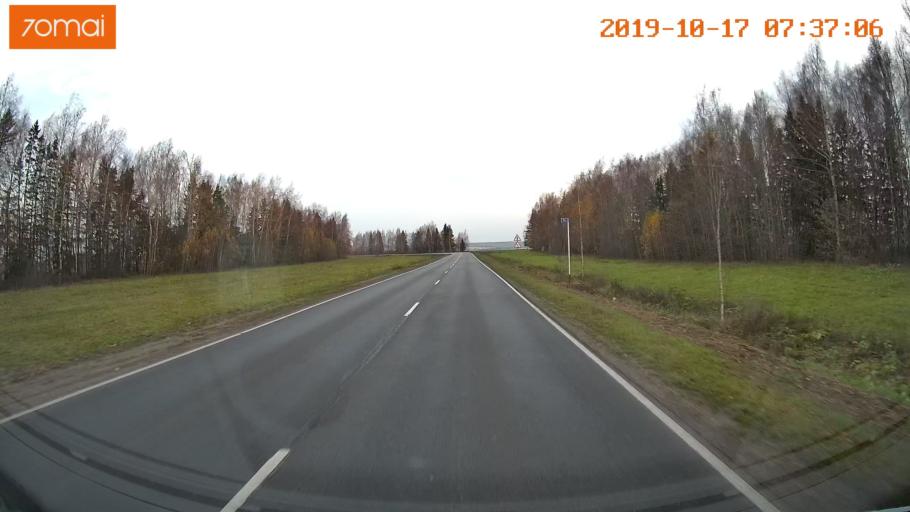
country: RU
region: Vladimir
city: Yur'yev-Pol'skiy
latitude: 56.4463
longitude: 39.9052
